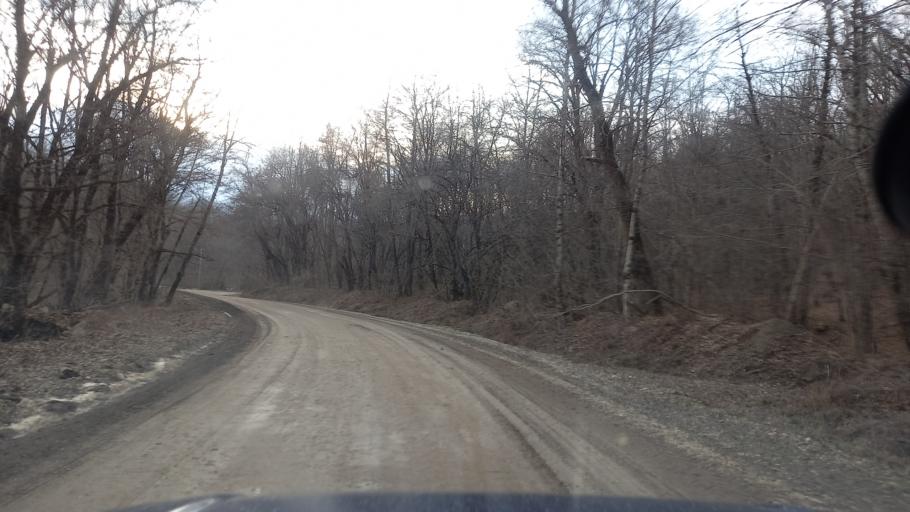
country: RU
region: Adygeya
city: Kamennomostskiy
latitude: 44.1417
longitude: 40.2697
